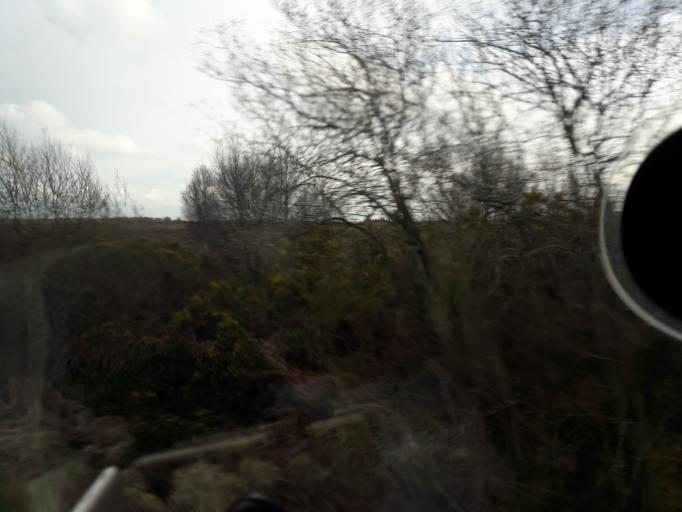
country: IE
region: Leinster
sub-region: An Iarmhi
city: Kinnegad
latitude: 53.4830
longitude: -7.0896
